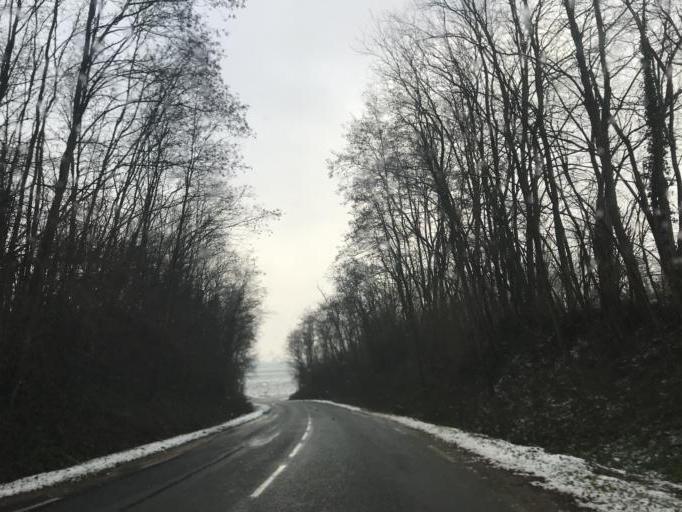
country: FR
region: Rhone-Alpes
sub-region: Departement de l'Ain
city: Miribel
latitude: 45.8487
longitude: 4.9588
